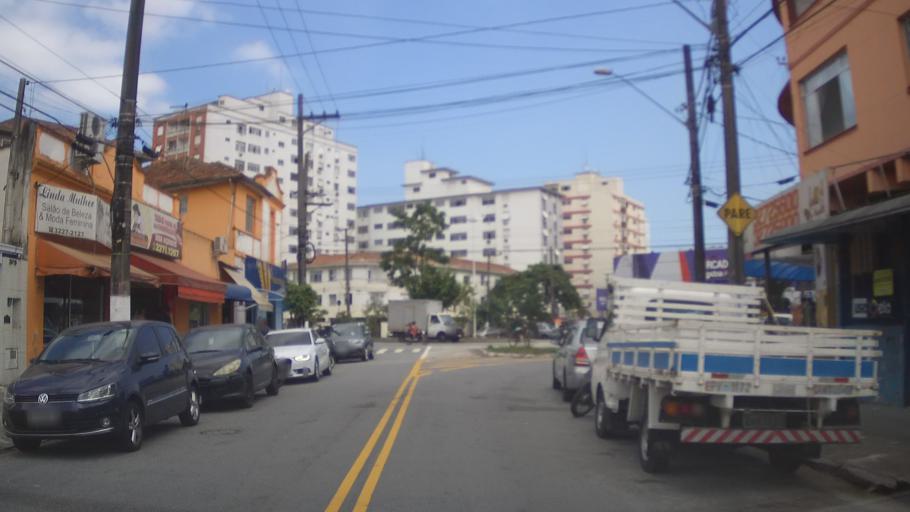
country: BR
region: Sao Paulo
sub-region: Santos
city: Santos
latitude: -23.9632
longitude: -46.3127
